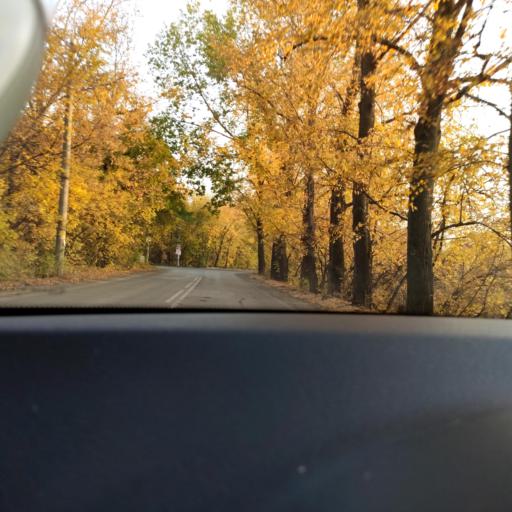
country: RU
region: Samara
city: Smyshlyayevka
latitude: 53.2518
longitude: 50.3684
